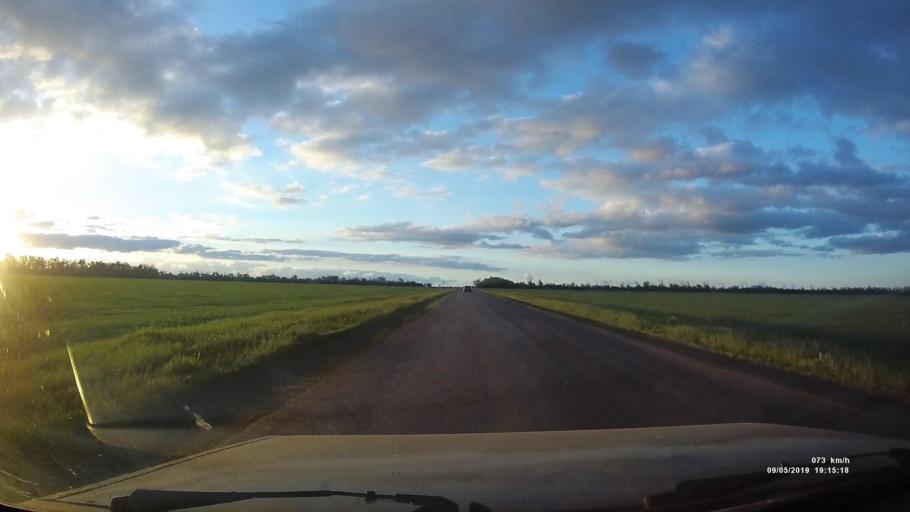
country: RU
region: Krasnodarskiy
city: Kanelovskaya
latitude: 46.7665
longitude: 39.2126
